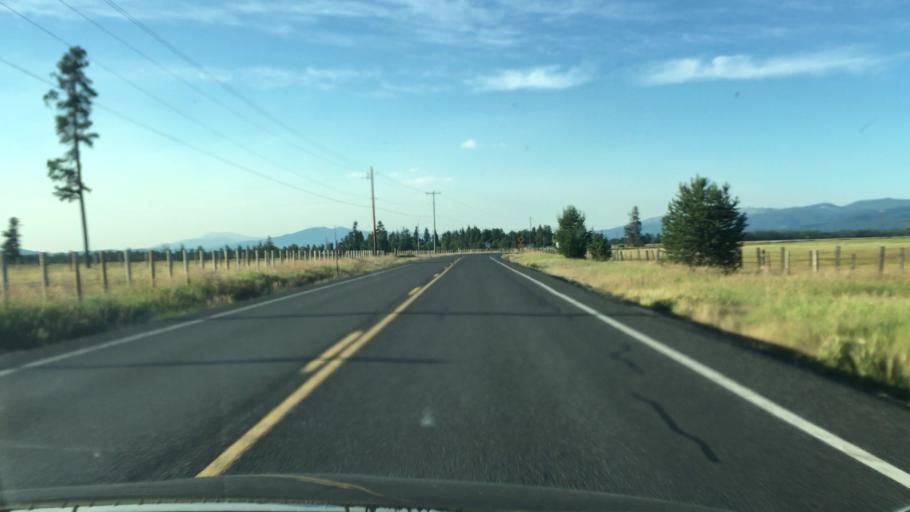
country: US
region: Idaho
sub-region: Valley County
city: McCall
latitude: 44.7702
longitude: -116.0781
